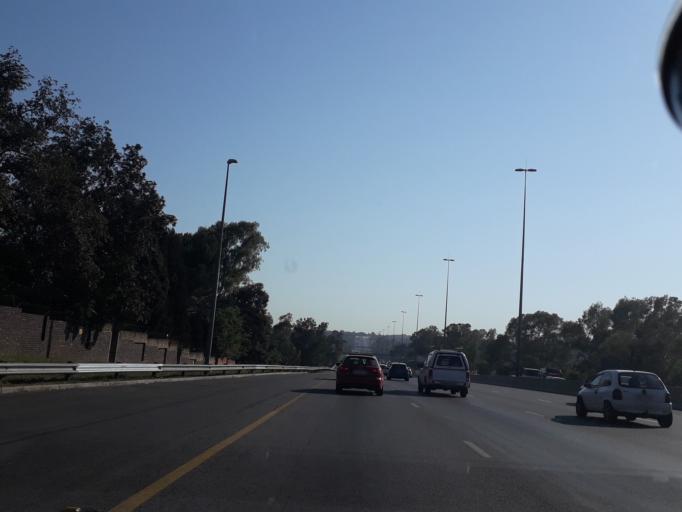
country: ZA
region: Gauteng
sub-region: City of Johannesburg Metropolitan Municipality
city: Diepsloot
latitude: -26.0587
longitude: 27.9866
